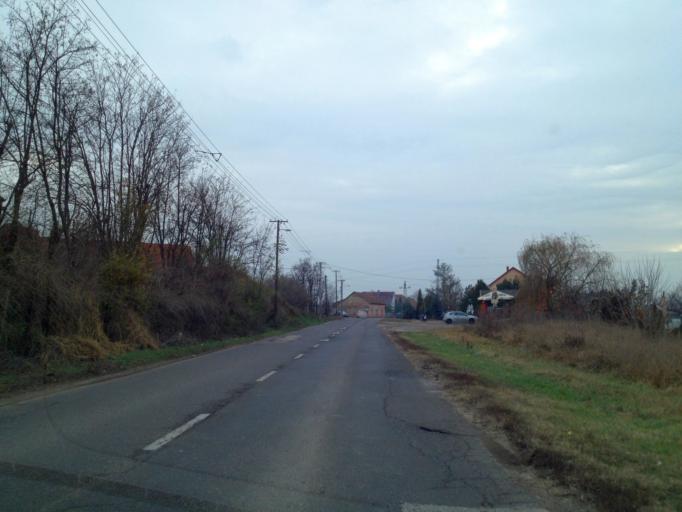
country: HU
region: Heves
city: Hatvan
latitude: 47.6825
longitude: 19.6879
